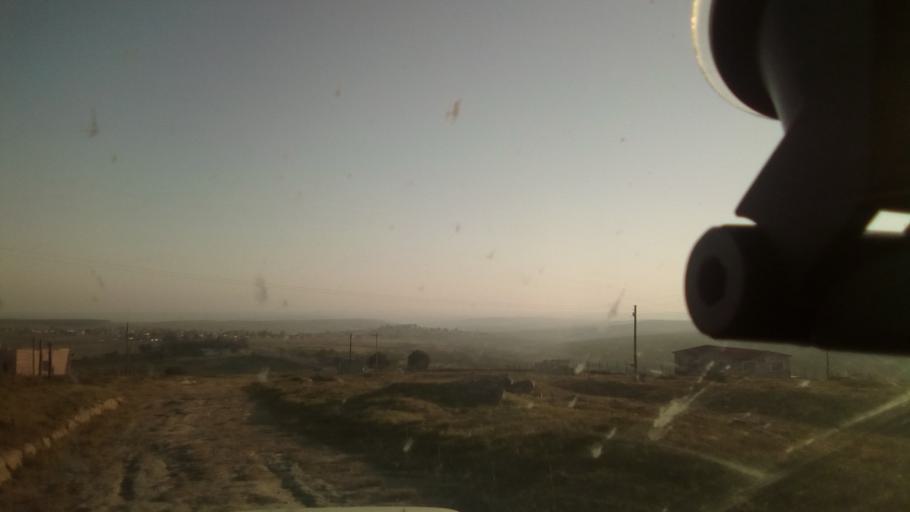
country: ZA
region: Eastern Cape
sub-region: Buffalo City Metropolitan Municipality
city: Bhisho
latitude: -32.9728
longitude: 27.2920
